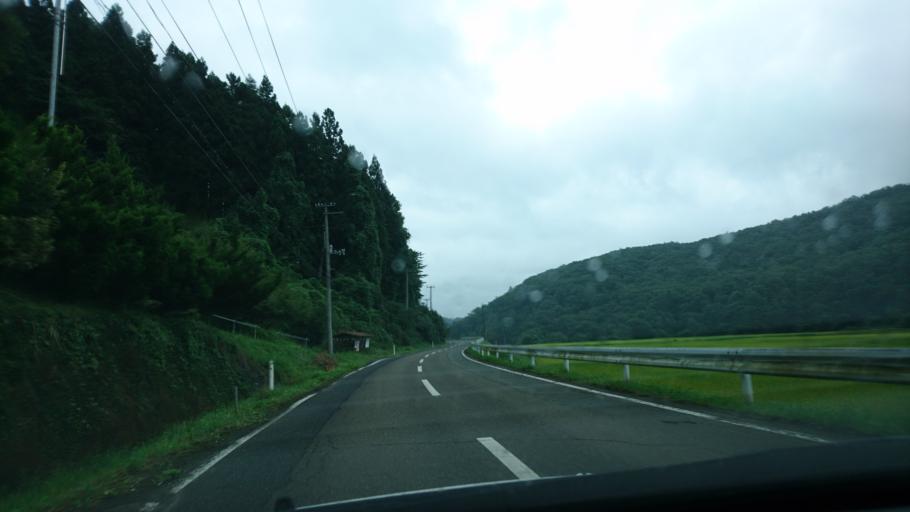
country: JP
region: Iwate
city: Ichinoseki
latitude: 38.9007
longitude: 141.0417
